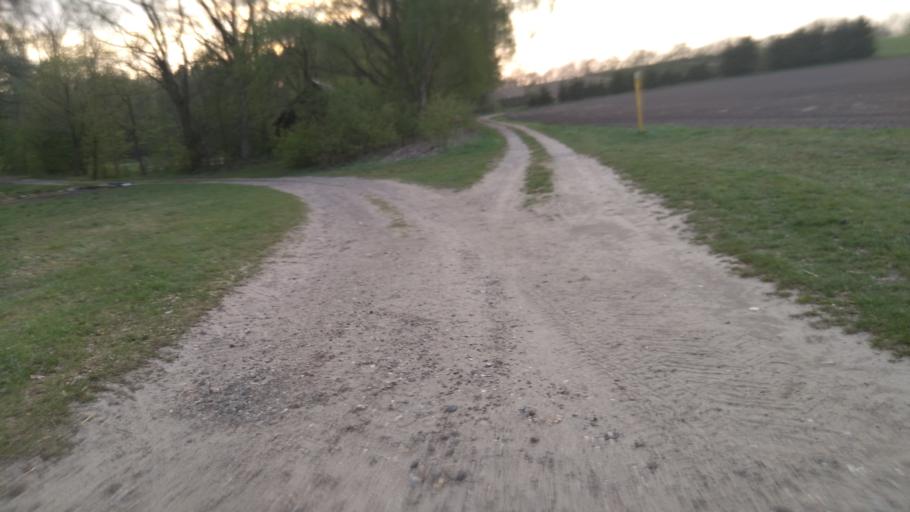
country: DE
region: Lower Saxony
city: Bliedersdorf
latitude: 53.4832
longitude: 9.5552
